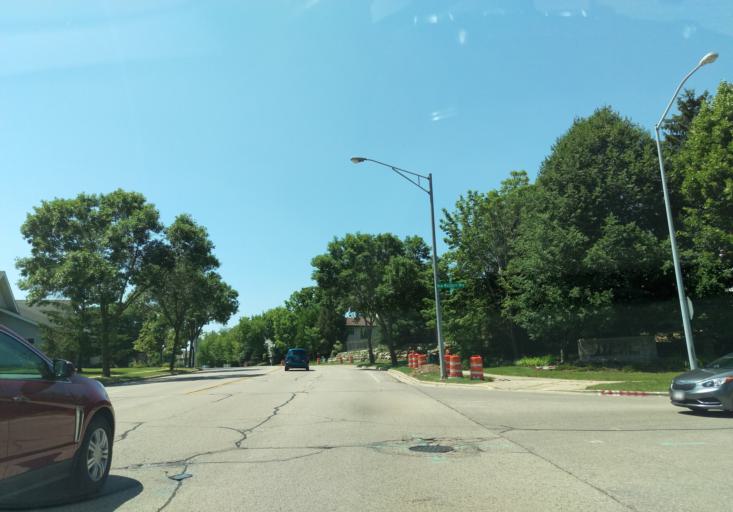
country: US
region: Wisconsin
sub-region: Dane County
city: Middleton
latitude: 43.0435
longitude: -89.5042
